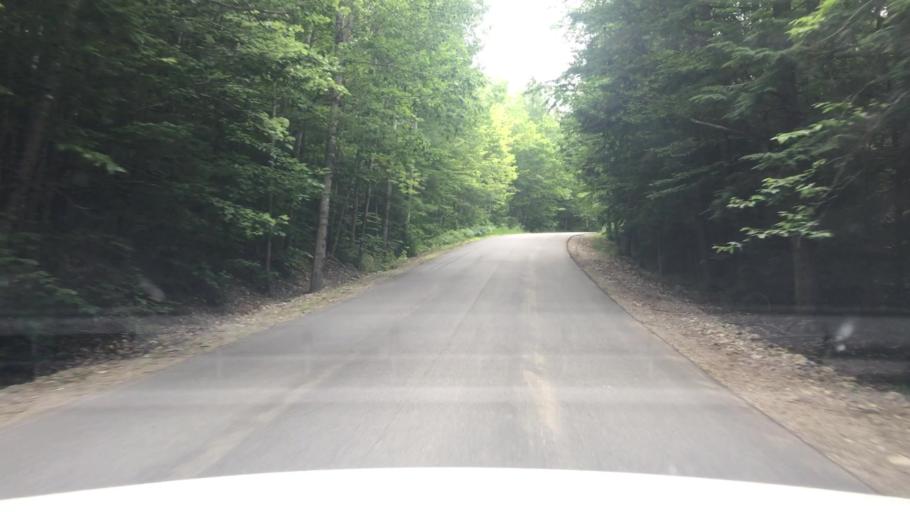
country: US
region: Maine
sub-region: Kennebec County
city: Albion
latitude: 44.4539
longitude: -69.3176
